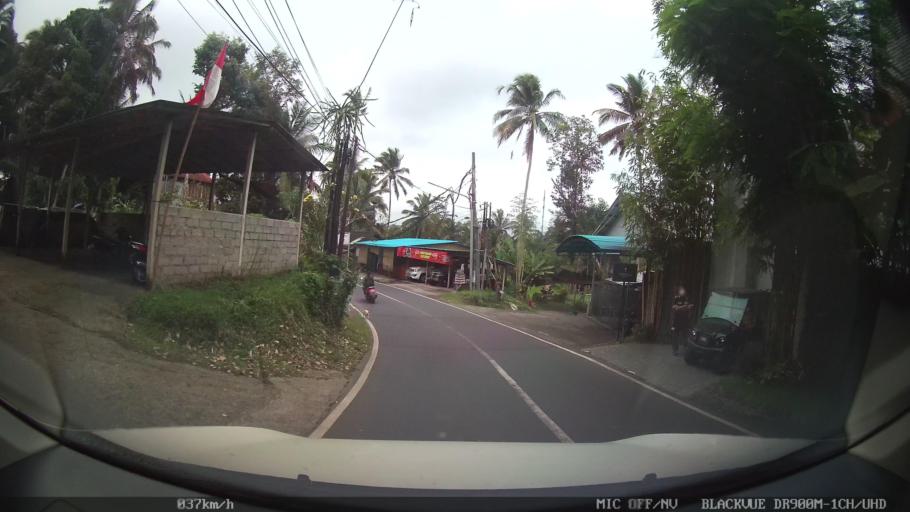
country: ID
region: Bali
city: Banjar Triwangsakeliki
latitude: -8.4481
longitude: 115.2682
